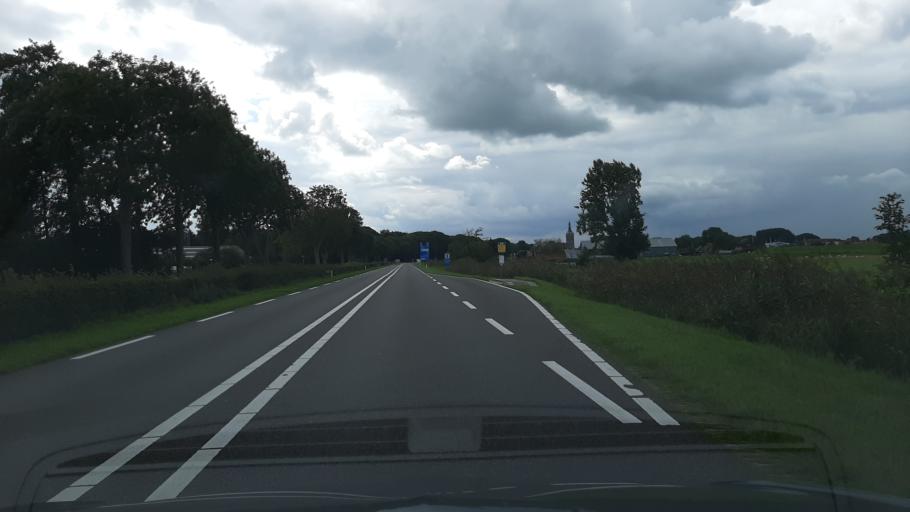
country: NL
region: Overijssel
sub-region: Gemeente Zwartewaterland
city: Hasselt
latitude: 52.6003
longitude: 6.0971
